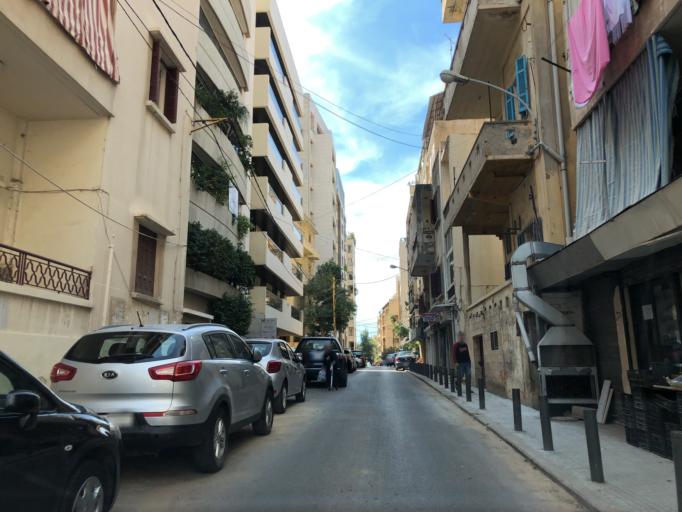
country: LB
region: Beyrouth
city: Beirut
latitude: 33.8859
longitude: 35.5190
